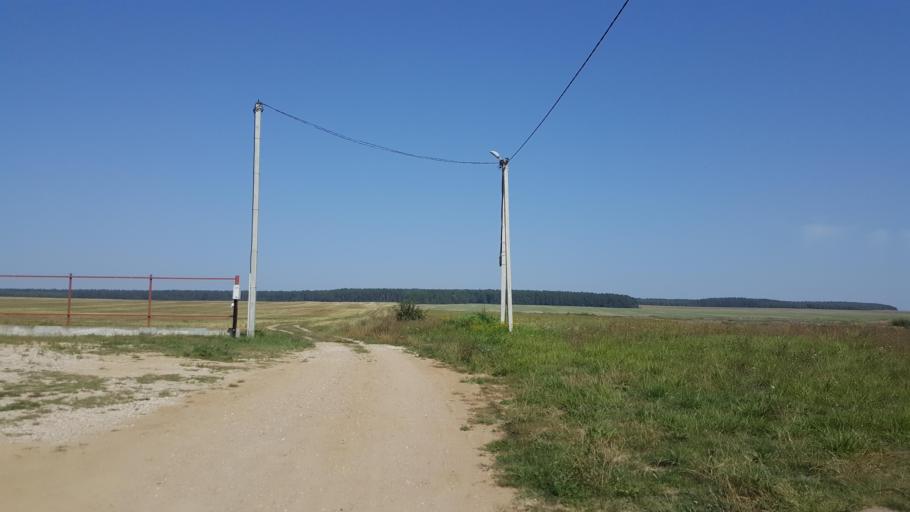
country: BY
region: Brest
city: Vysokaye
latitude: 52.4141
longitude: 23.4672
